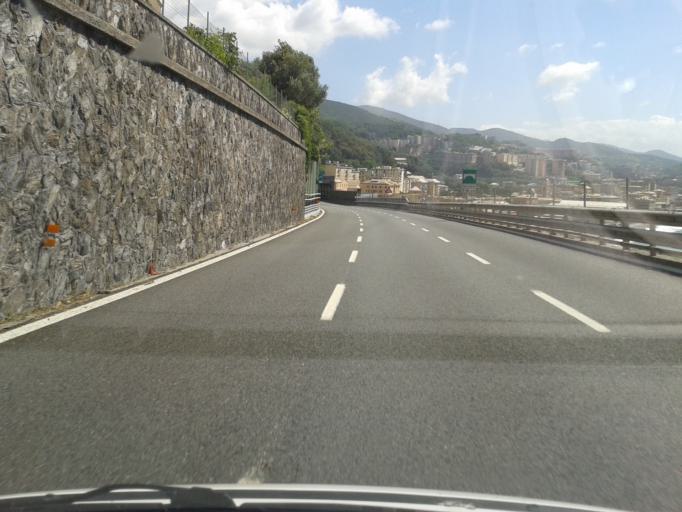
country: IT
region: Liguria
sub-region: Provincia di Genova
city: Mele
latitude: 44.4257
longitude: 8.7386
